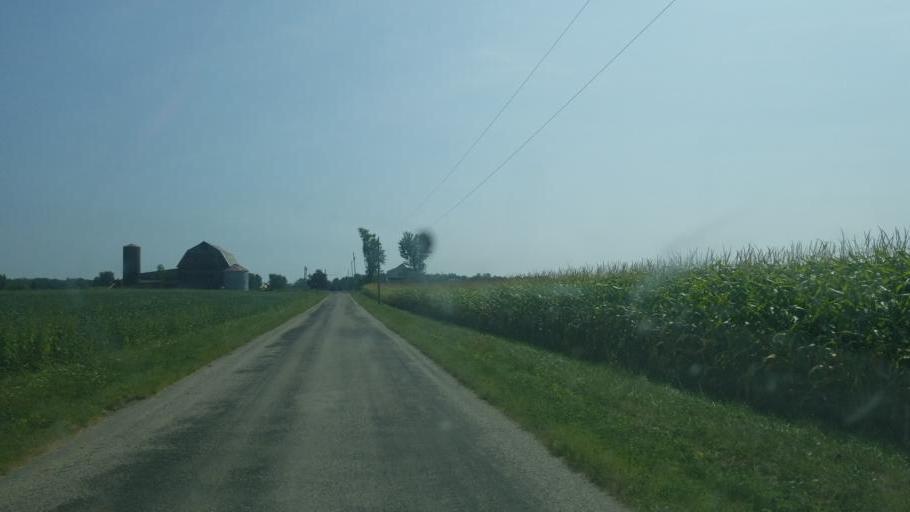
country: US
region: Ohio
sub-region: Crawford County
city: Crestline
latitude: 40.8208
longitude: -82.7063
